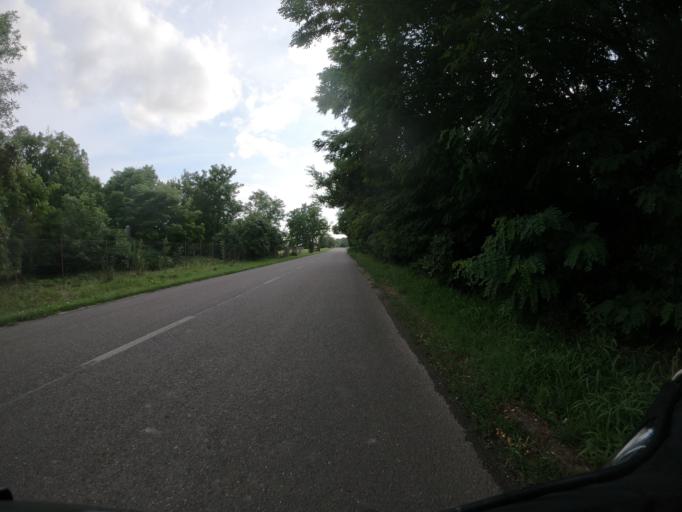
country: HU
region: Borsod-Abauj-Zemplen
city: Mezokeresztes
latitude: 47.8260
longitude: 20.7665
